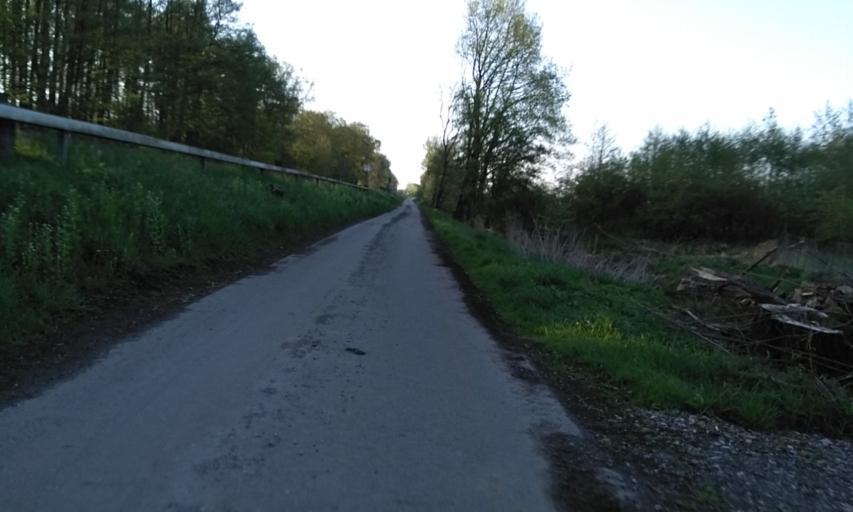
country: DE
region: Lower Saxony
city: Dollern
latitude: 53.5358
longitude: 9.5640
